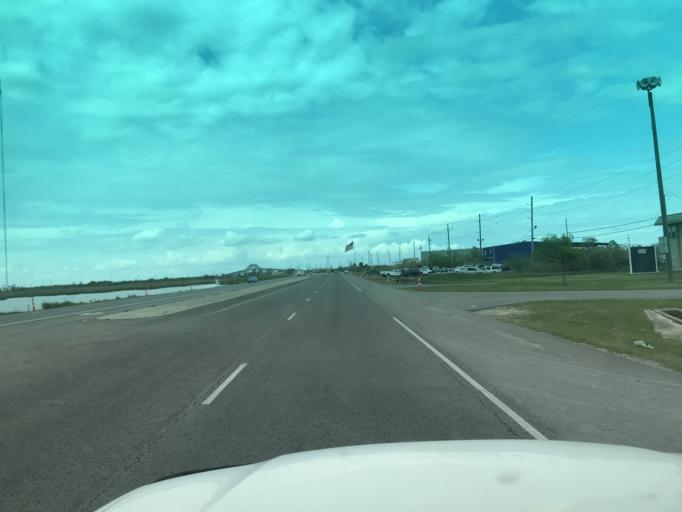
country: US
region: Louisiana
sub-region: Saint Bernard Parish
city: Chalmette
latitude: 29.9740
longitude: -89.9482
